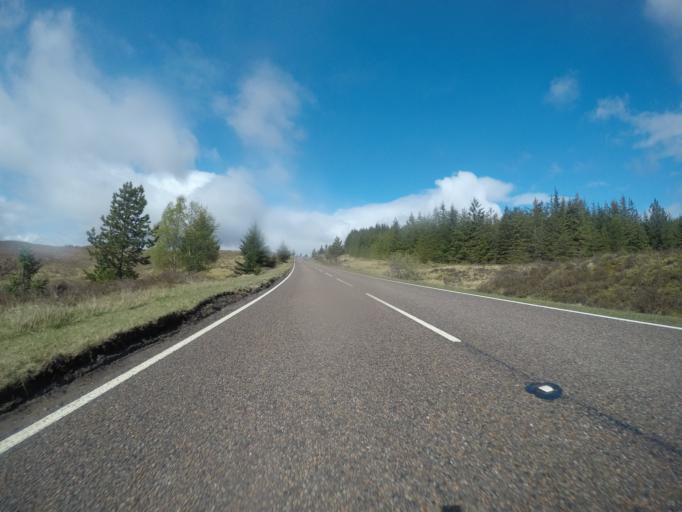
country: GB
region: Scotland
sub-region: Highland
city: Spean Bridge
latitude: 57.0933
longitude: -4.9879
